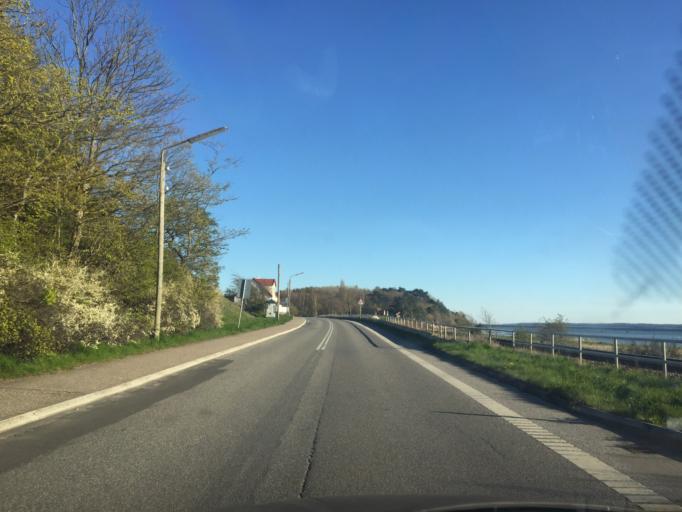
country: DK
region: Capital Region
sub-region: Halsnaes Kommune
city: Frederiksvaerk
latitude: 55.9577
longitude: 12.0203
